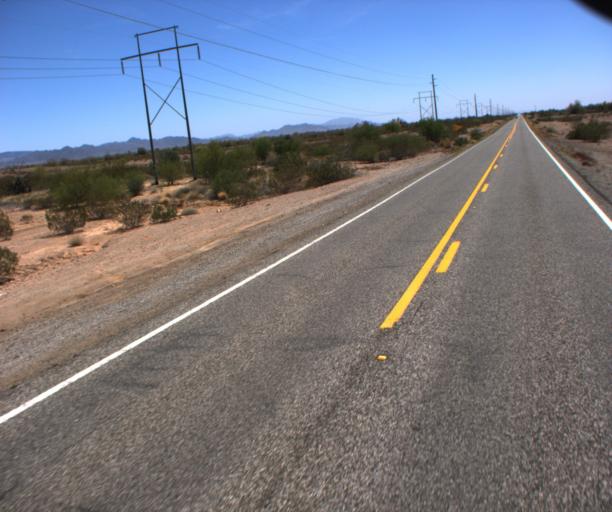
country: US
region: Arizona
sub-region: La Paz County
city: Quartzsite
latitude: 33.7598
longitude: -114.2170
